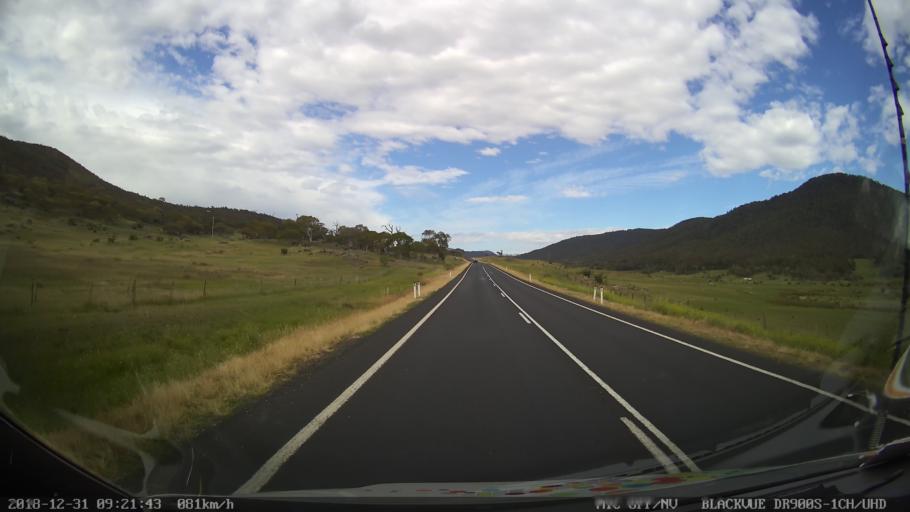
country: AU
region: New South Wales
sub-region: Snowy River
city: Jindabyne
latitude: -36.4307
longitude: 148.5576
